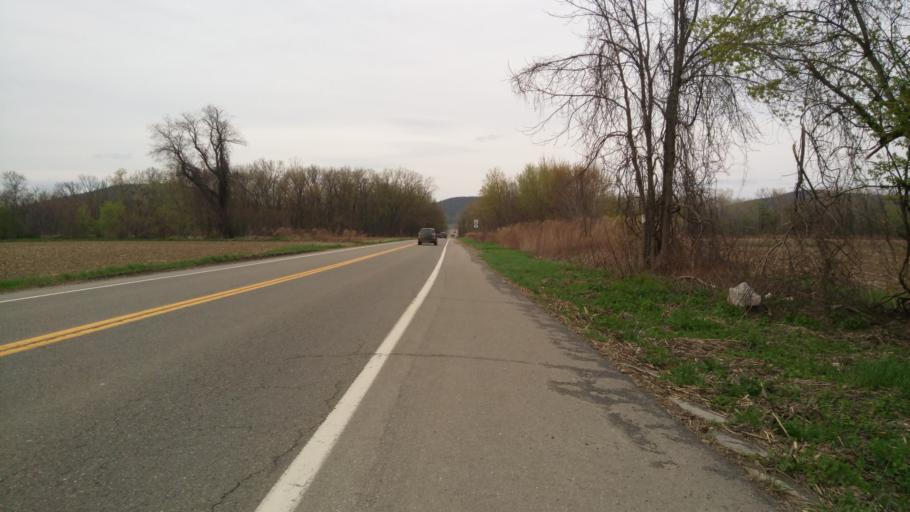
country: US
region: New York
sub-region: Chemung County
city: Southport
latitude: 42.0202
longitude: -76.7227
